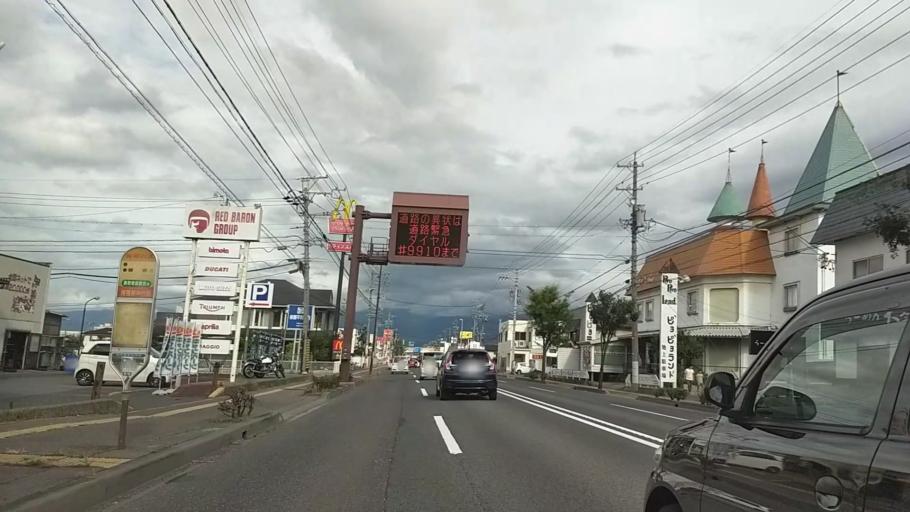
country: JP
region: Nagano
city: Nagano-shi
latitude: 36.6551
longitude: 138.2361
